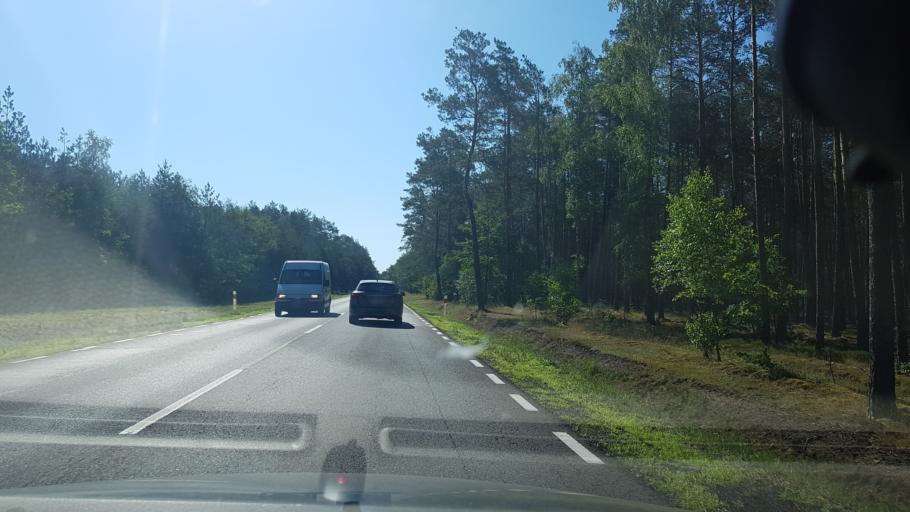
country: PL
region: Masovian Voivodeship
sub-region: Powiat wyszkowski
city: Branszczyk
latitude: 52.5604
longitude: 21.5747
